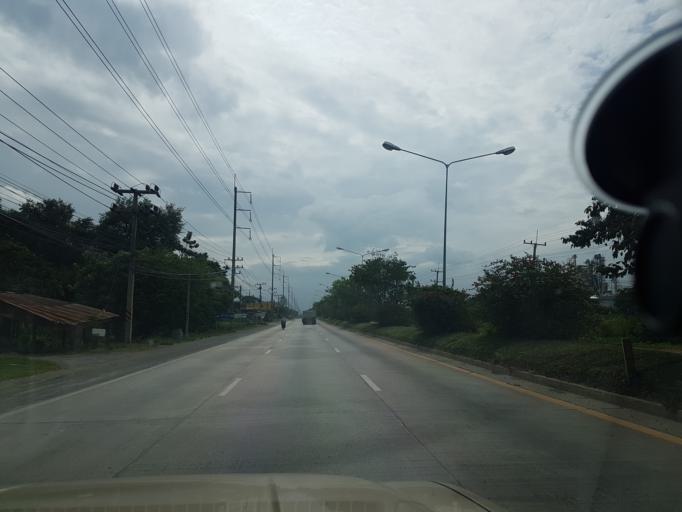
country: TH
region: Sara Buri
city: Phra Phutthabat
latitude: 14.7106
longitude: 100.8308
